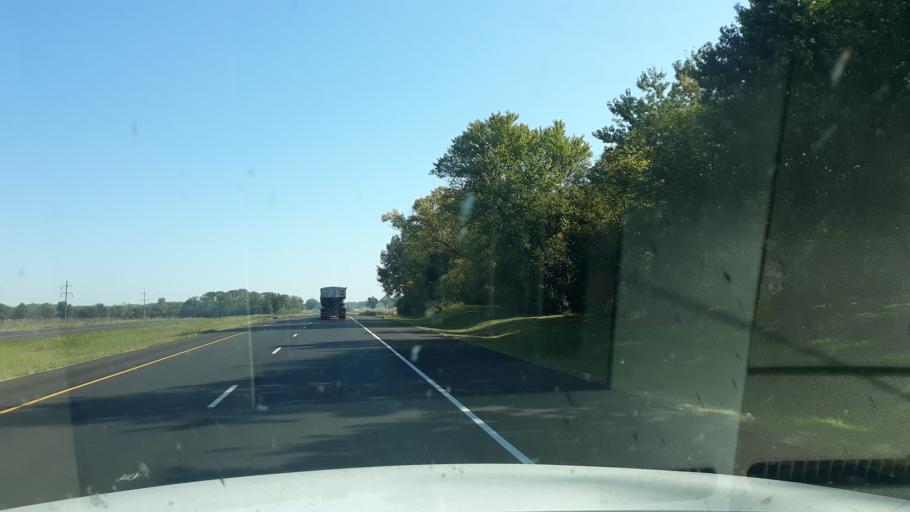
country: US
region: Illinois
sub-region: Saline County
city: Eldorado
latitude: 37.7922
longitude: -88.4769
